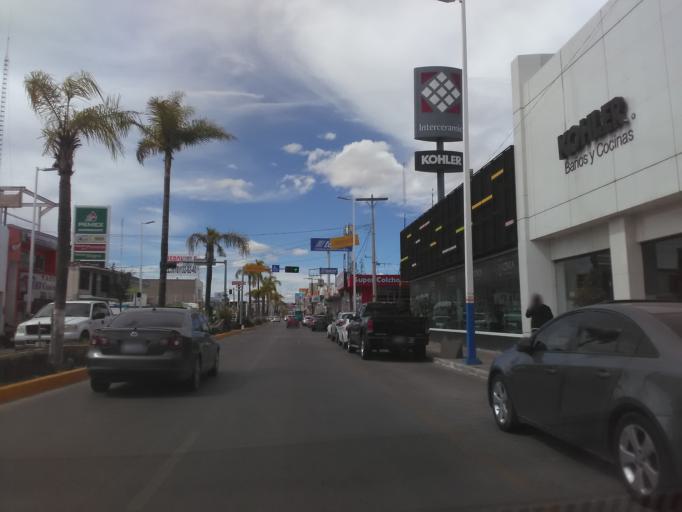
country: MX
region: Durango
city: Victoria de Durango
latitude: 24.0282
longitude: -104.6490
